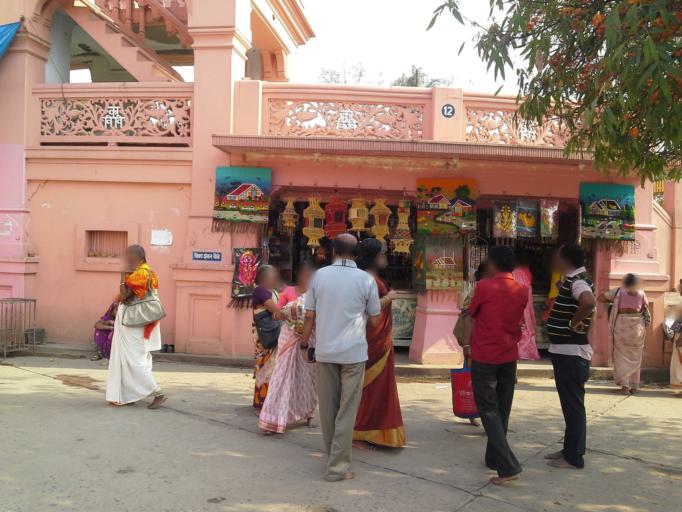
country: IN
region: Uttar Pradesh
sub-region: Varanasi
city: Ramnagar
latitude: 25.2658
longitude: 82.9892
